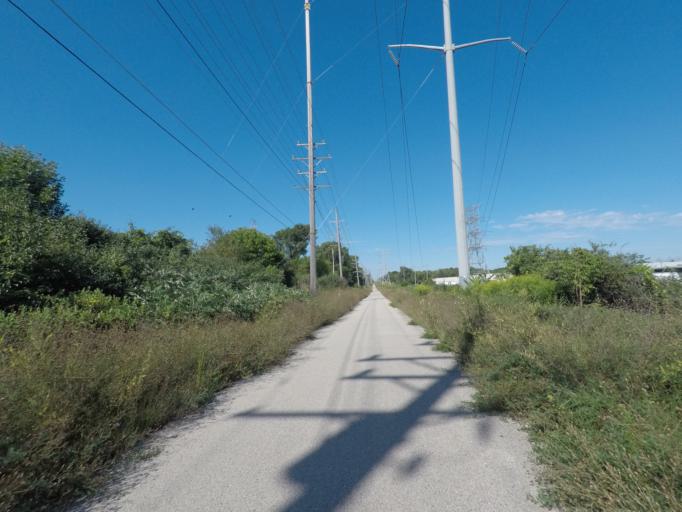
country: US
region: Wisconsin
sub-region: Milwaukee County
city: West Allis
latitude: 43.0103
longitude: -88.0496
